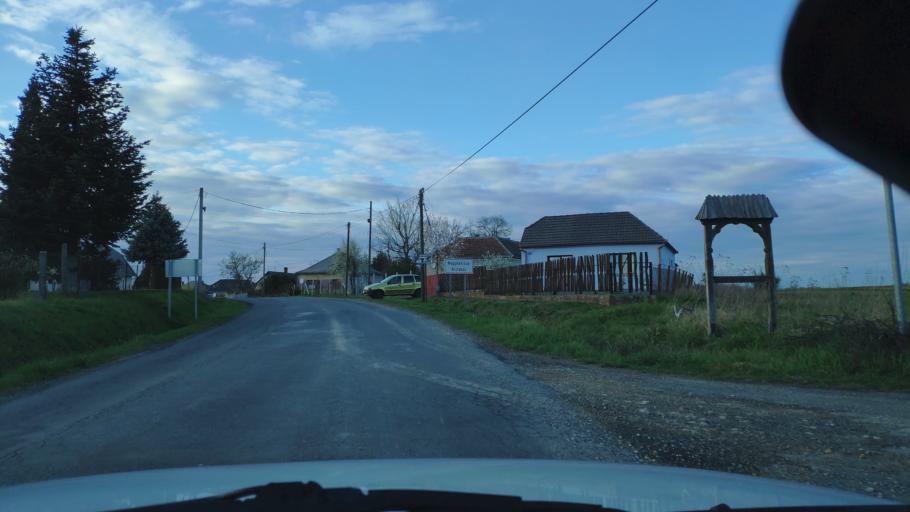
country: HU
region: Zala
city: Nagykanizsa
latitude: 46.4305
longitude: 17.0618
